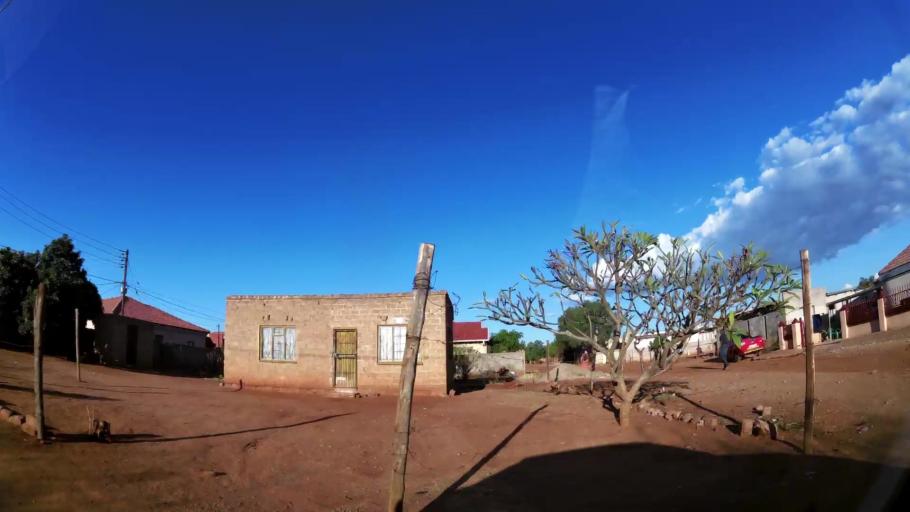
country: ZA
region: Limpopo
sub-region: Waterberg District Municipality
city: Mokopane
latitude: -24.1497
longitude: 28.9949
